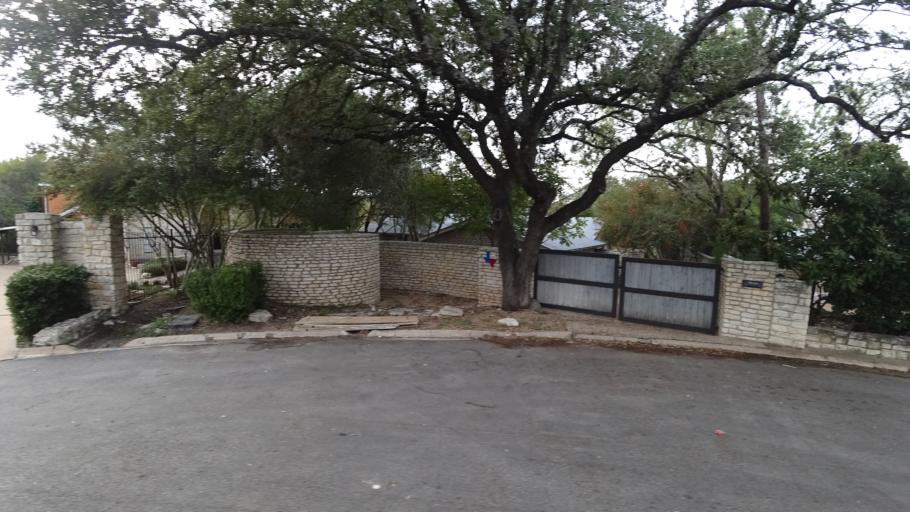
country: US
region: Texas
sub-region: Travis County
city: Hudson Bend
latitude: 30.3894
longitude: -97.8927
